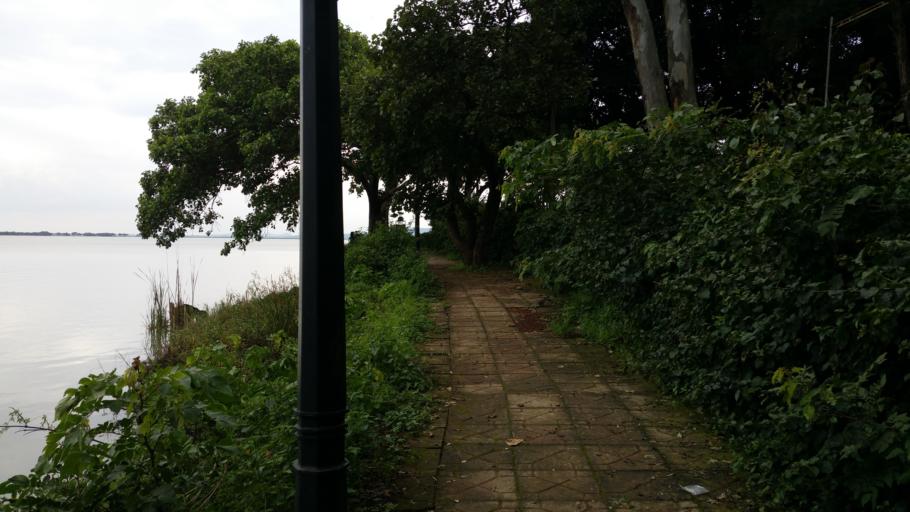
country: ET
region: Amhara
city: Bahir Dar
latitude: 11.6037
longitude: 37.3941
